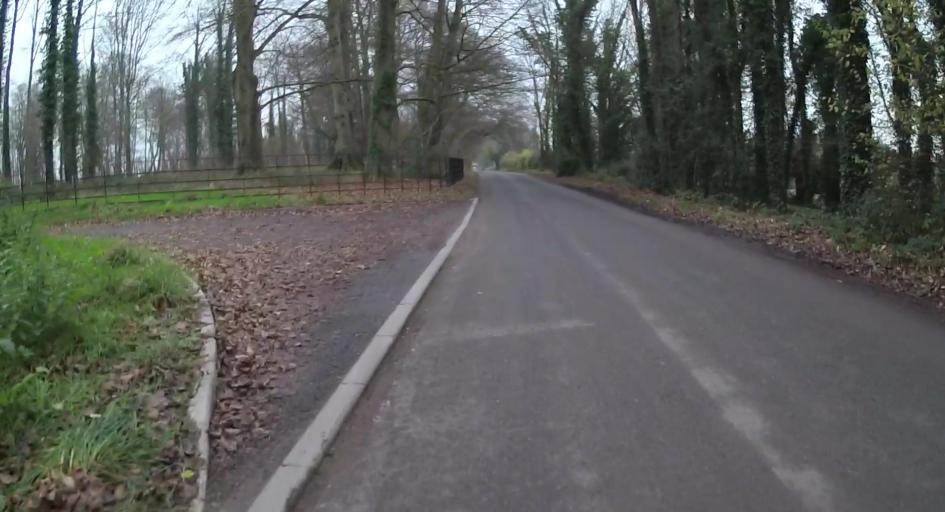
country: GB
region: England
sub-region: Hampshire
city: Kings Worthy
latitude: 51.1298
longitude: -1.2112
